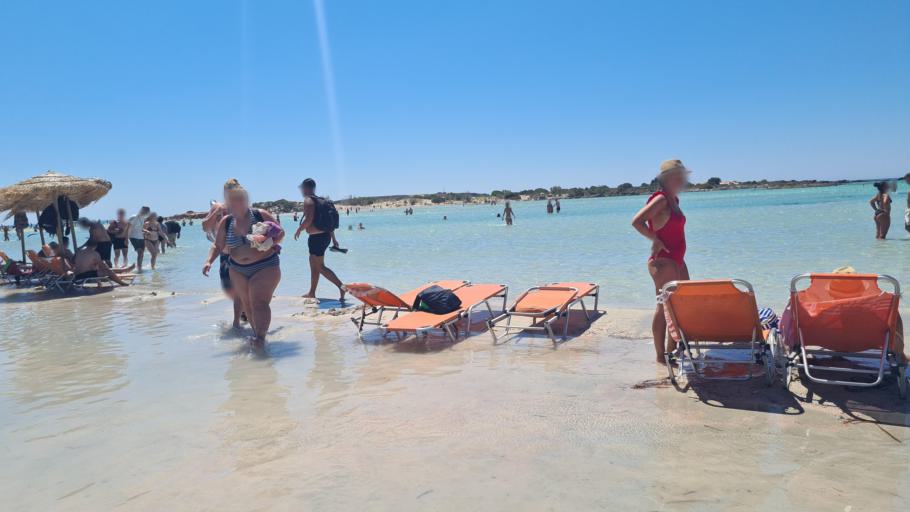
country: GR
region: Crete
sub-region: Nomos Chanias
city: Palaiochora
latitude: 35.2711
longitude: 23.5412
